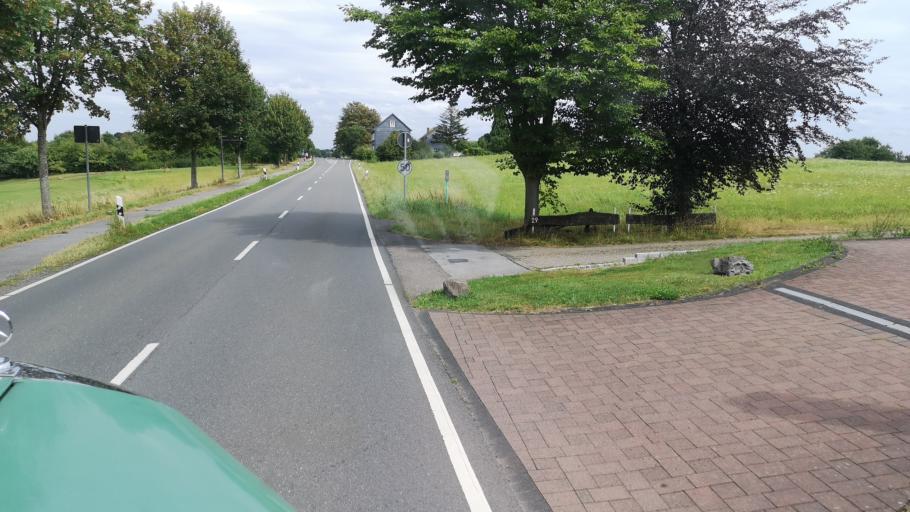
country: DE
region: North Rhine-Westphalia
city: Wermelskirchen
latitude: 51.1335
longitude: 7.2736
